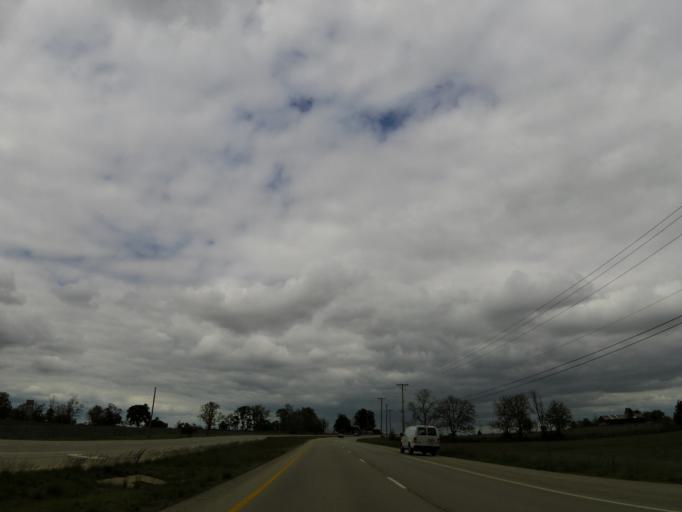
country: US
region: Kentucky
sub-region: Scott County
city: Georgetown
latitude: 38.1619
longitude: -84.6099
